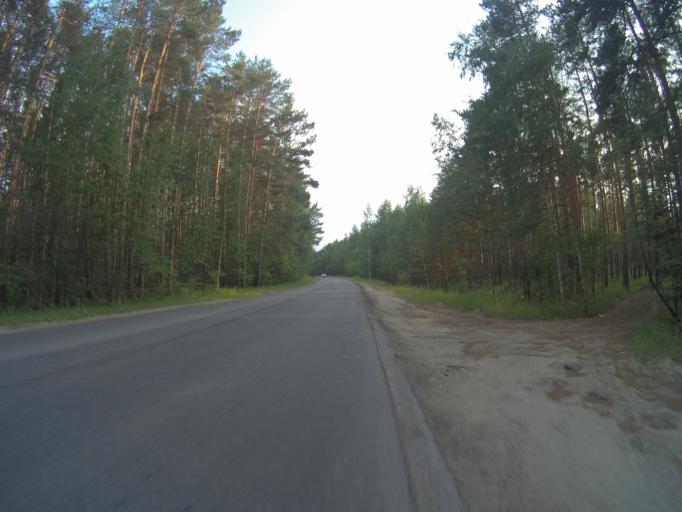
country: RU
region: Vladimir
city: Kommunar
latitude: 56.1304
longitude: 40.4864
